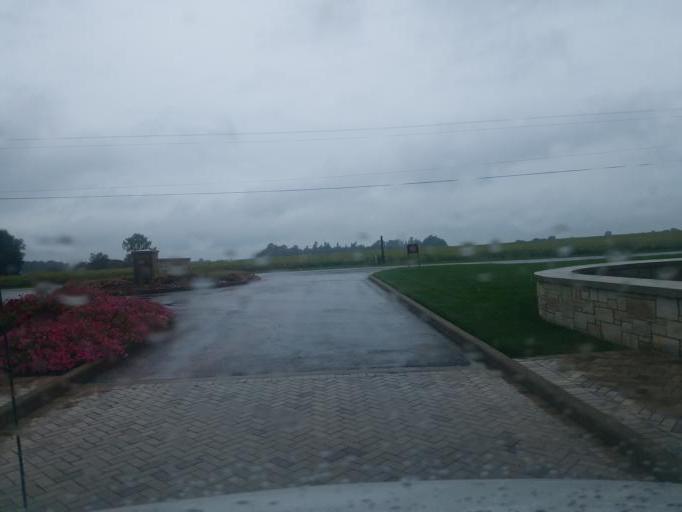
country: US
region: Ohio
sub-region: Wayne County
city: Rittman
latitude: 41.0037
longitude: -81.8148
